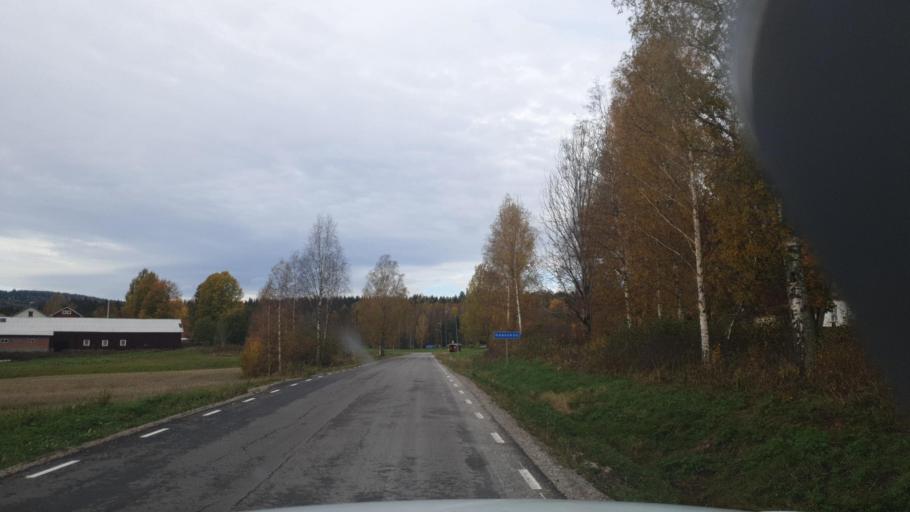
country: SE
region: Vaermland
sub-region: Arvika Kommun
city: Arvika
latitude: 59.7500
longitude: 12.8264
